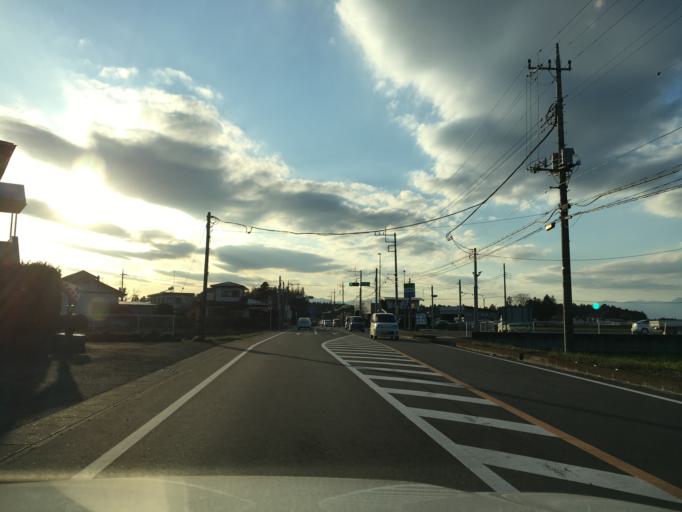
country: JP
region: Tochigi
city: Otawara
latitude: 36.8593
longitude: 140.0968
